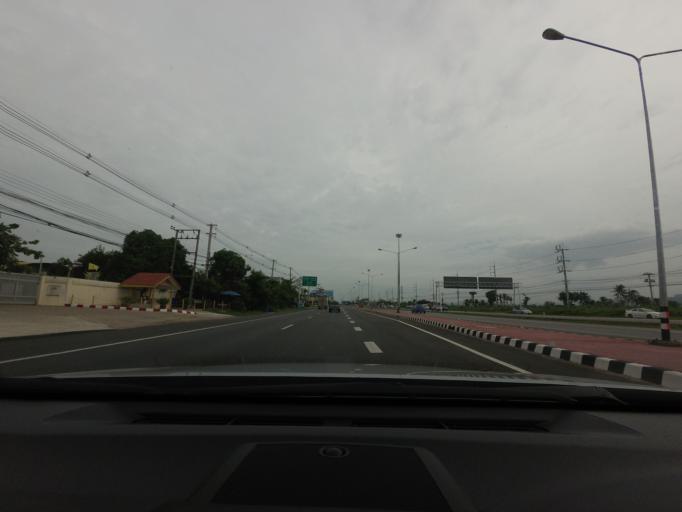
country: TH
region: Ratchaburi
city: Pak Tho
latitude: 13.3344
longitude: 99.8304
